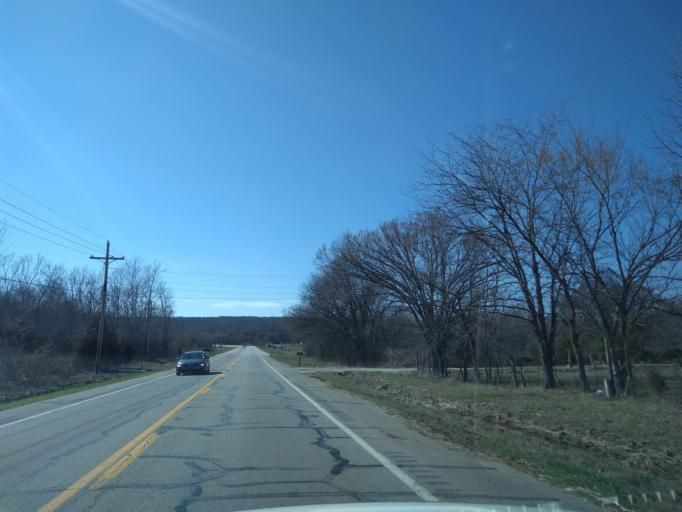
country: US
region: Arkansas
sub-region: Washington County
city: Prairie Grove
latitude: 35.9602
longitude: -94.3611
